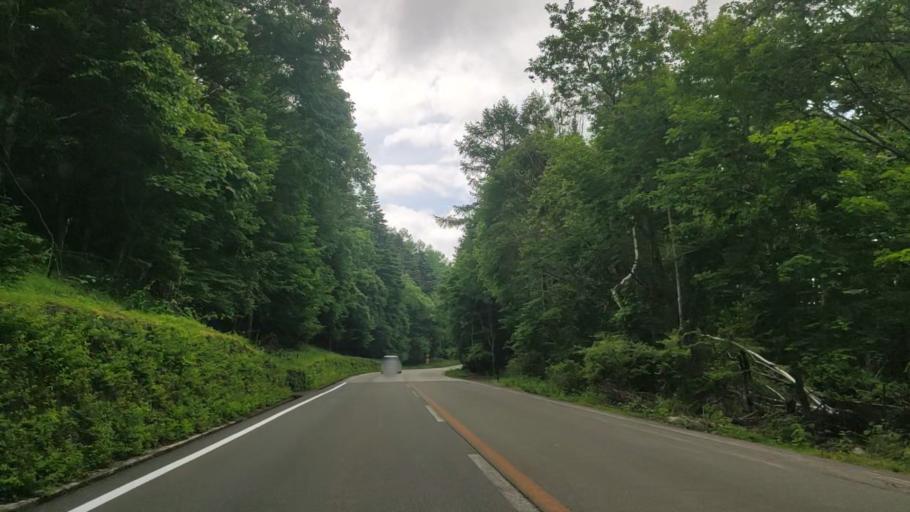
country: JP
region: Yamanashi
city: Fujikawaguchiko
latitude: 35.4147
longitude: 138.7333
